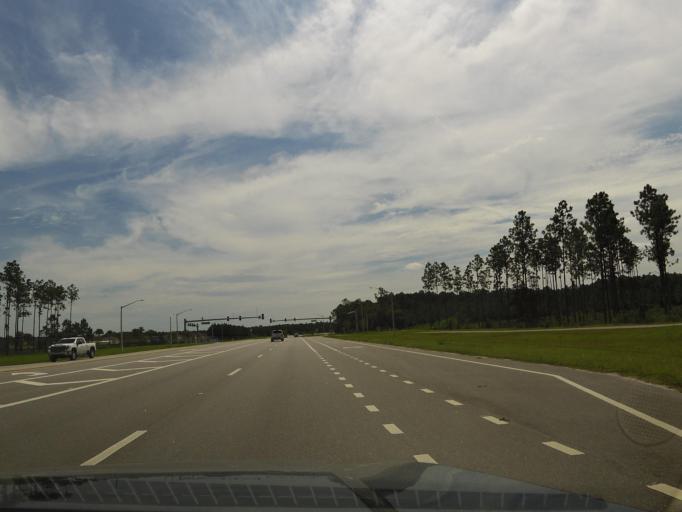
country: US
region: Florida
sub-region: Saint Johns County
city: Fruit Cove
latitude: 30.0178
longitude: -81.5127
